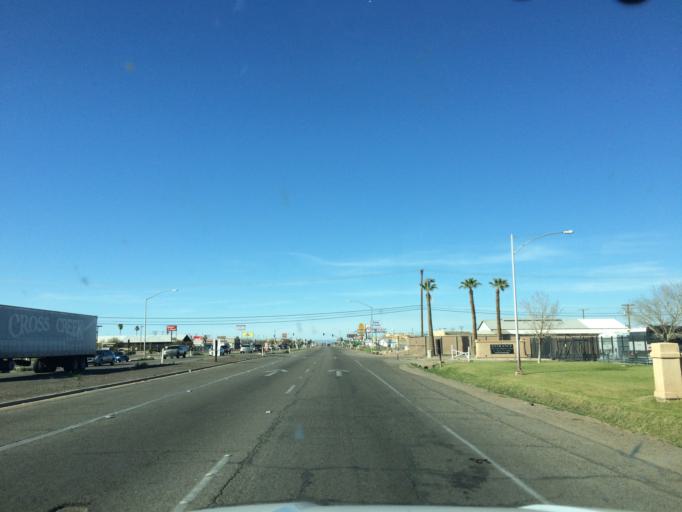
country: US
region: California
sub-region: Imperial County
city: El Centro
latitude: 32.8027
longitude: -115.5698
